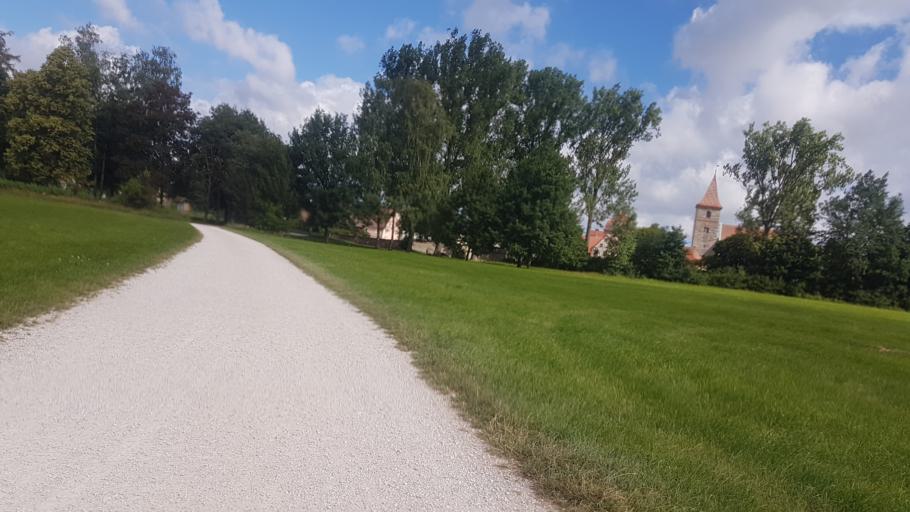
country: DE
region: Bavaria
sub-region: Regierungsbezirk Mittelfranken
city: Ornbau
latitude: 49.1725
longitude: 10.6565
